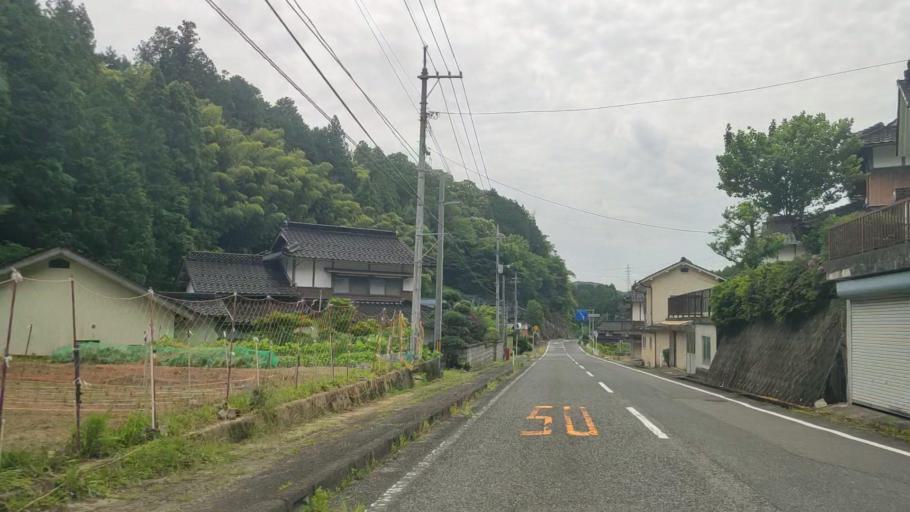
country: JP
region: Hyogo
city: Yamazakicho-nakabirose
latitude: 35.0940
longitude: 134.2826
